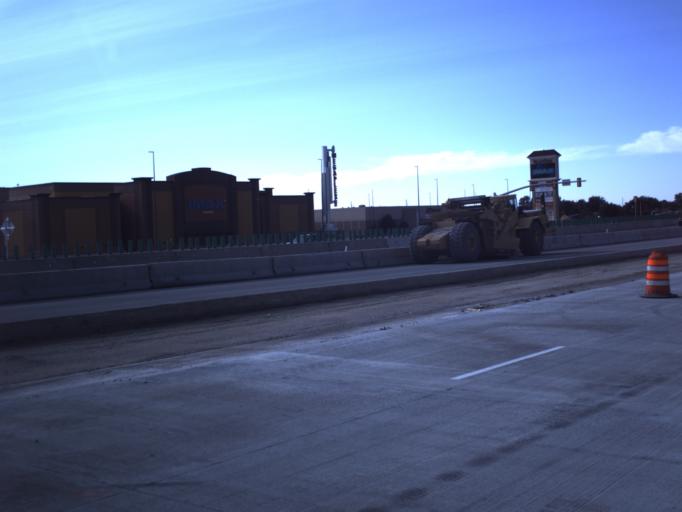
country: US
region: Utah
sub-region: Salt Lake County
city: Taylorsville
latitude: 40.6927
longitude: -111.9518
